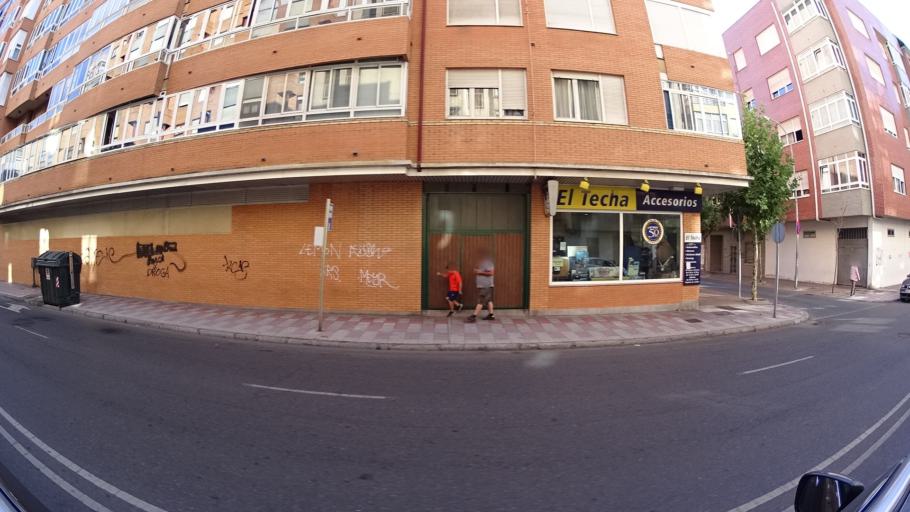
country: ES
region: Castille and Leon
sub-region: Provincia de Leon
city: Leon
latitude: 42.5900
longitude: -5.5628
